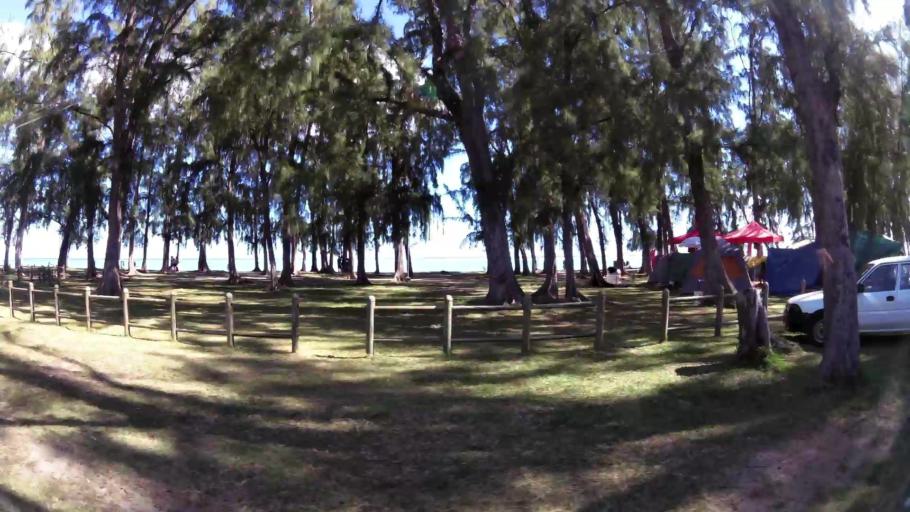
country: MU
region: Black River
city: Flic en Flac
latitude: -20.2885
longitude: 57.3637
